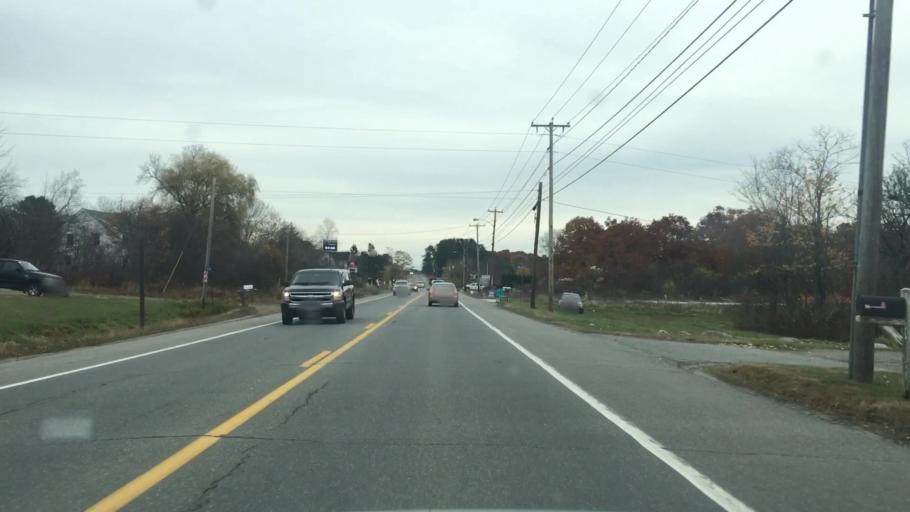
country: US
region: Maine
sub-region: Waldo County
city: Belfast
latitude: 44.4296
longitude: -68.9739
